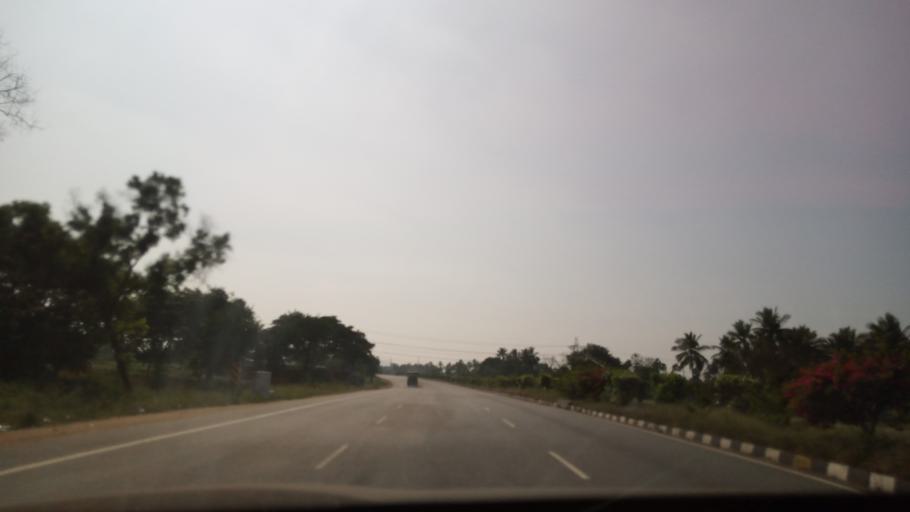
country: IN
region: Tamil Nadu
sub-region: Vellore
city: Jolarpettai
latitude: 12.6058
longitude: 78.5465
